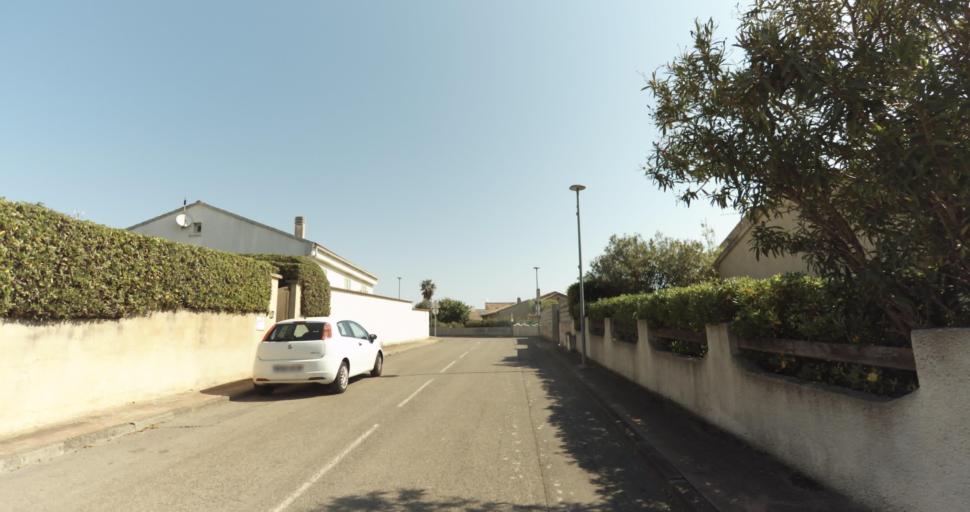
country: FR
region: Corsica
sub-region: Departement de la Haute-Corse
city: Biguglia
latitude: 42.6248
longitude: 9.4278
